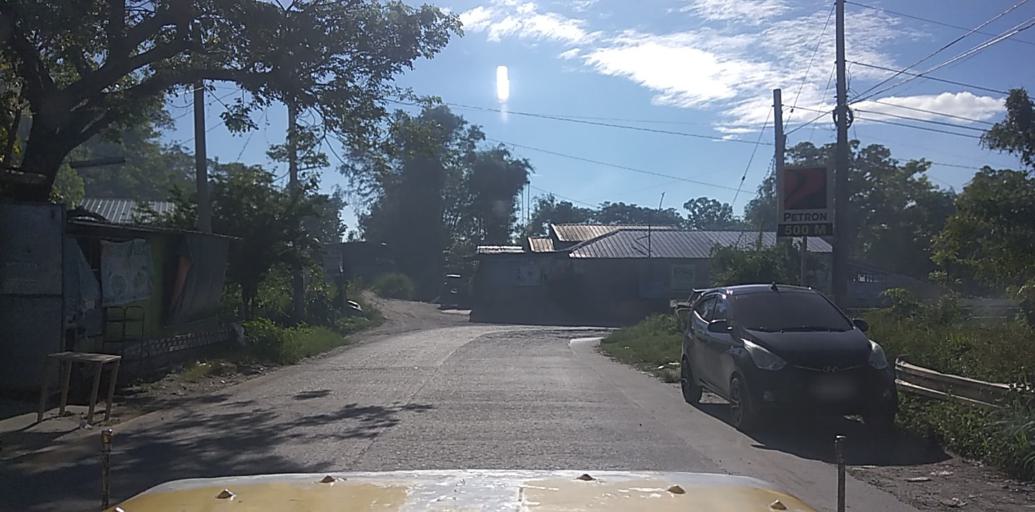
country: PH
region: Central Luzon
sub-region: Province of Pampanga
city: Anao
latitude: 15.1190
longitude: 120.7030
